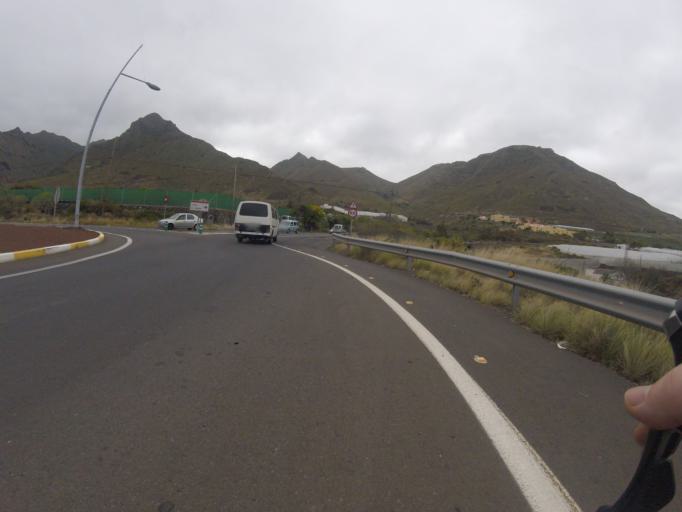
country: ES
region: Canary Islands
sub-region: Provincia de Santa Cruz de Tenerife
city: Tegueste
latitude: 28.5485
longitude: -16.3501
